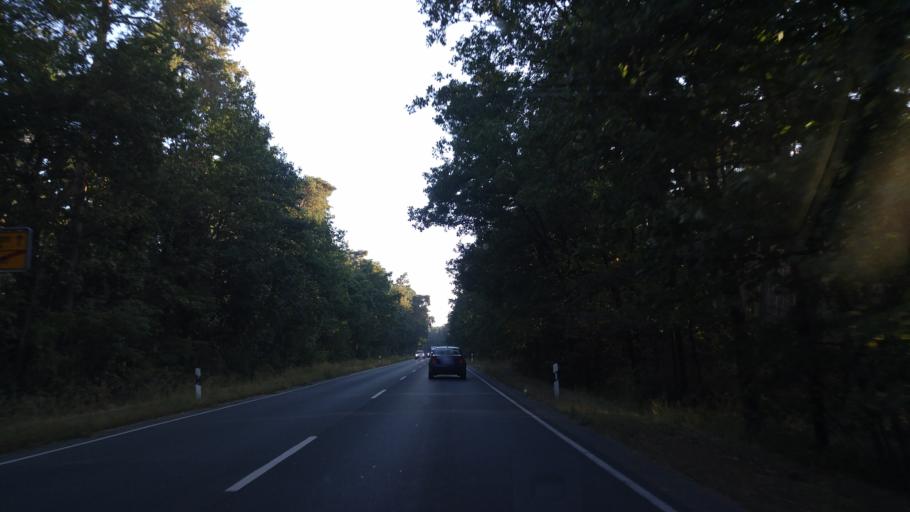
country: DE
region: Bavaria
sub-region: Regierungsbezirk Mittelfranken
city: Furth
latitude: 49.5287
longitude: 10.9797
